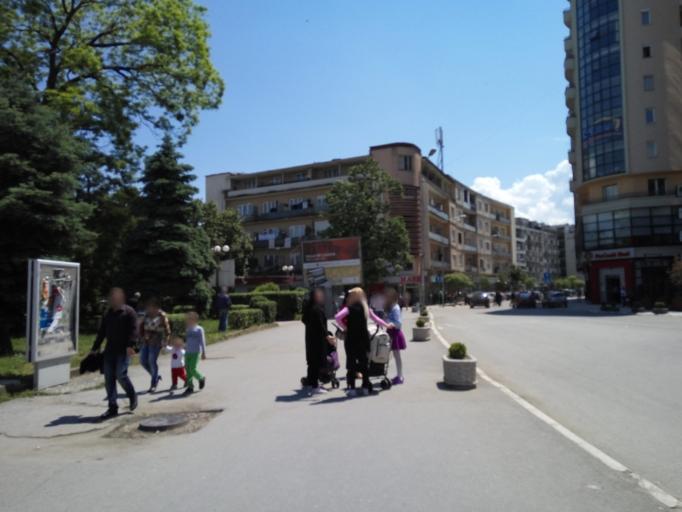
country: XK
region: Gjakova
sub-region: Komuna e Gjakoves
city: Gjakove
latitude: 42.3837
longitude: 20.4299
